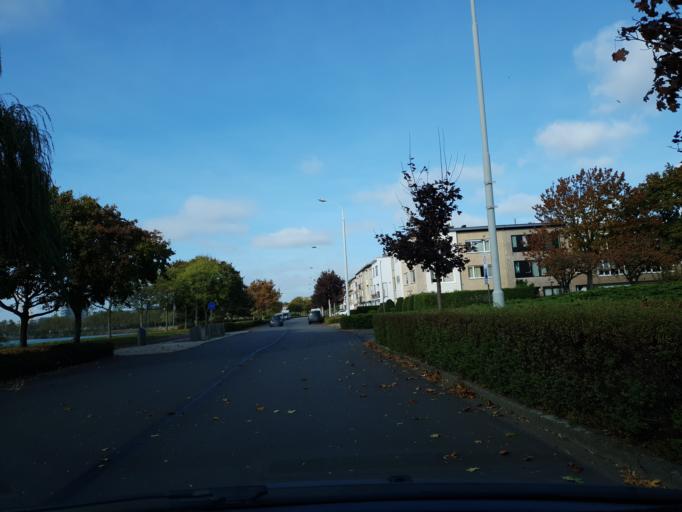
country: BE
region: Flanders
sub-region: Provincie Antwerpen
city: Antwerpen
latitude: 51.2151
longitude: 4.3811
